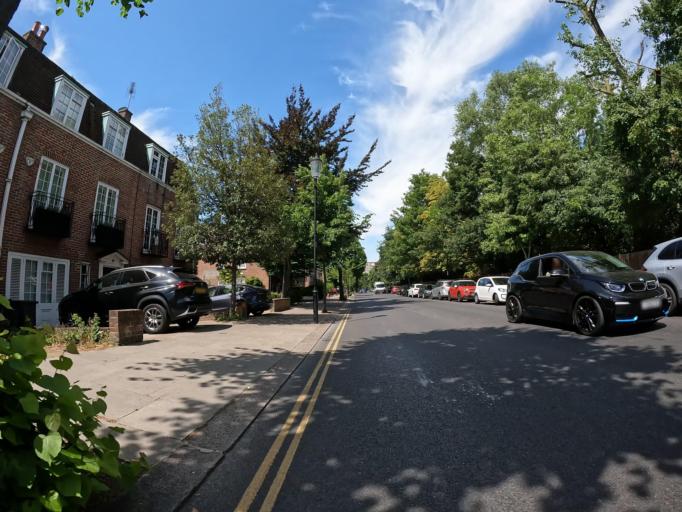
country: GB
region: England
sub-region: Greater London
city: Kensington
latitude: 51.5017
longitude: -0.2065
